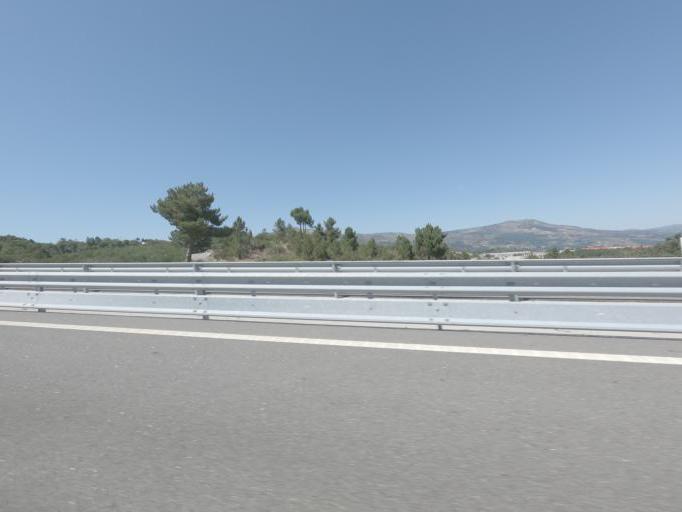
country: PT
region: Vila Real
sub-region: Santa Marta de Penaguiao
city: Santa Marta de Penaguiao
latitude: 41.2649
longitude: -7.8022
